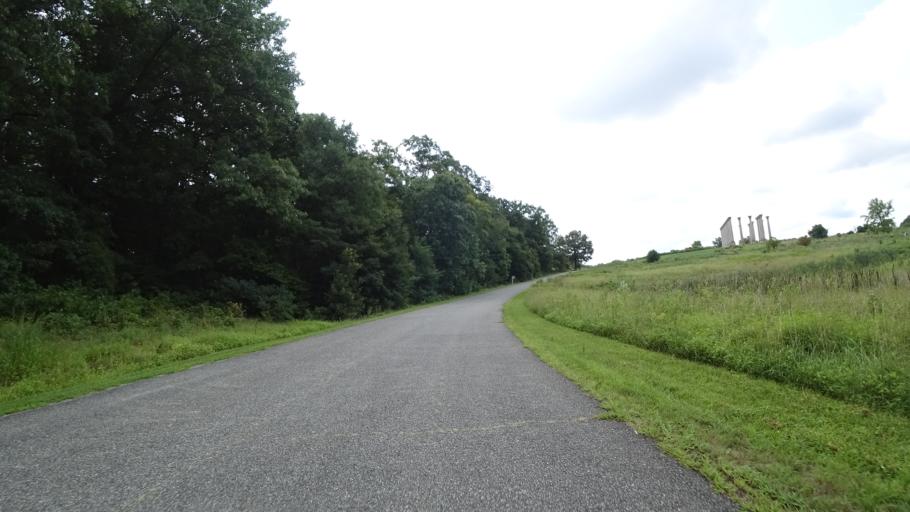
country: US
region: Maryland
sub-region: Prince George's County
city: Mount Rainier
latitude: 38.9118
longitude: -76.9675
